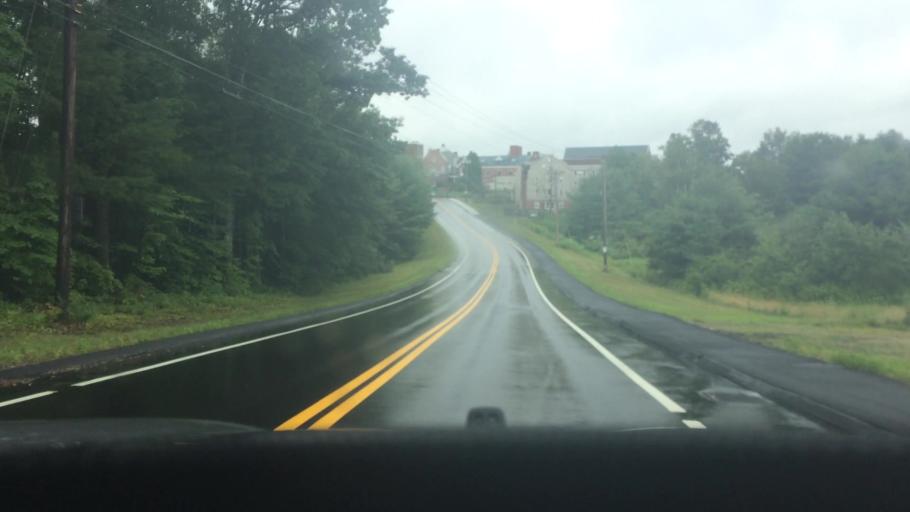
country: US
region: Massachusetts
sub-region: Worcester County
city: Gardner
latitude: 42.5879
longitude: -71.9835
